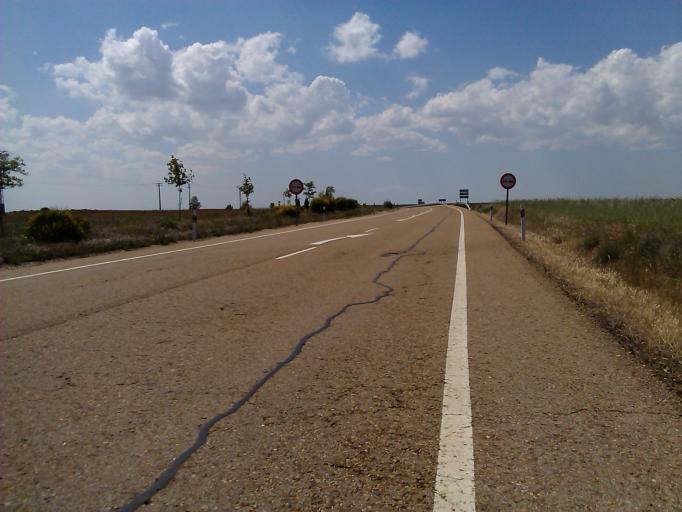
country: ES
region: Castille and Leon
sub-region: Provincia de Palencia
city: Ledigos
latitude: 42.3477
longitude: -4.8555
